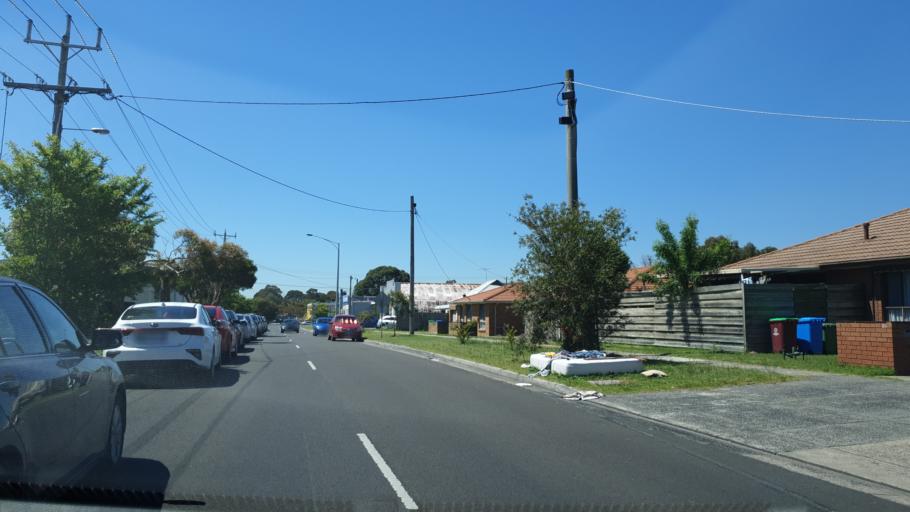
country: AU
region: Victoria
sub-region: Casey
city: Cranbourne
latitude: -38.1015
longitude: 145.2806
